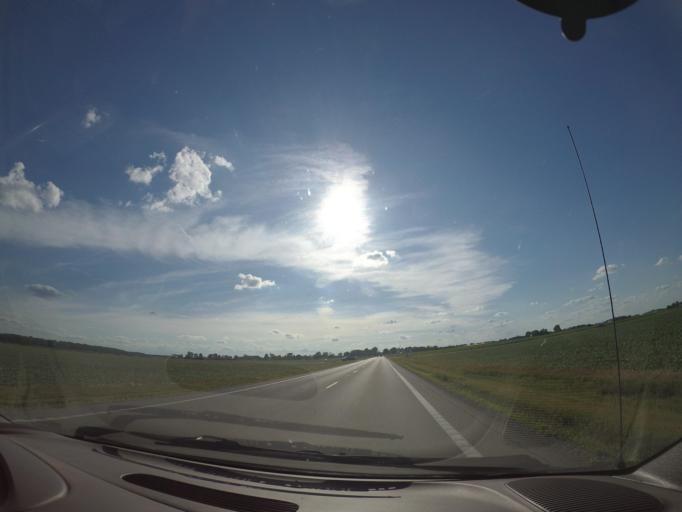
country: US
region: Ohio
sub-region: Henry County
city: Napoleon
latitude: 41.4330
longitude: -84.2270
